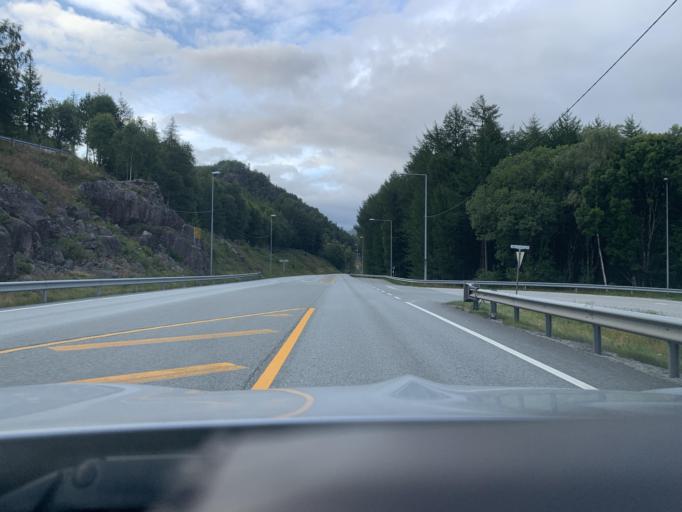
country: NO
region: Rogaland
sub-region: Bjerkreim
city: Vikesa
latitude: 58.5945
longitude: 6.0792
